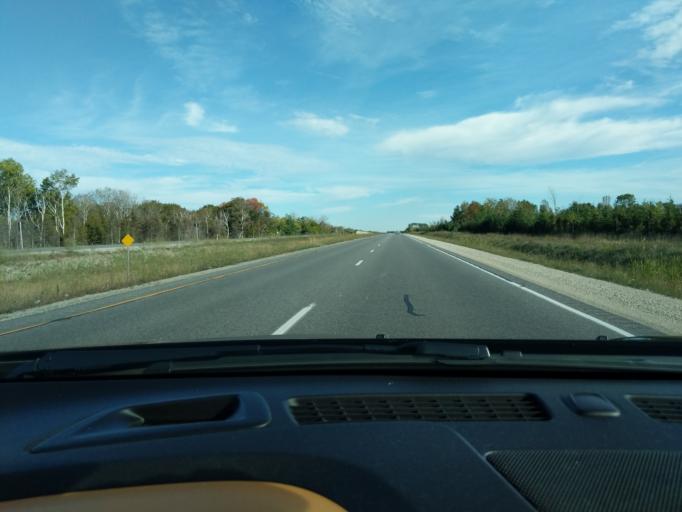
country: CA
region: Ontario
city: Collingwood
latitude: 44.4809
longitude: -80.1671
